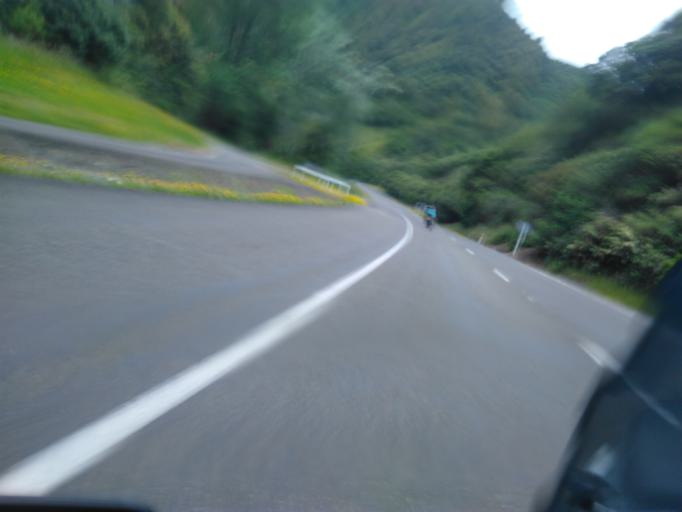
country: NZ
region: Bay of Plenty
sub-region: Opotiki District
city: Opotiki
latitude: -38.3404
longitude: 177.4258
